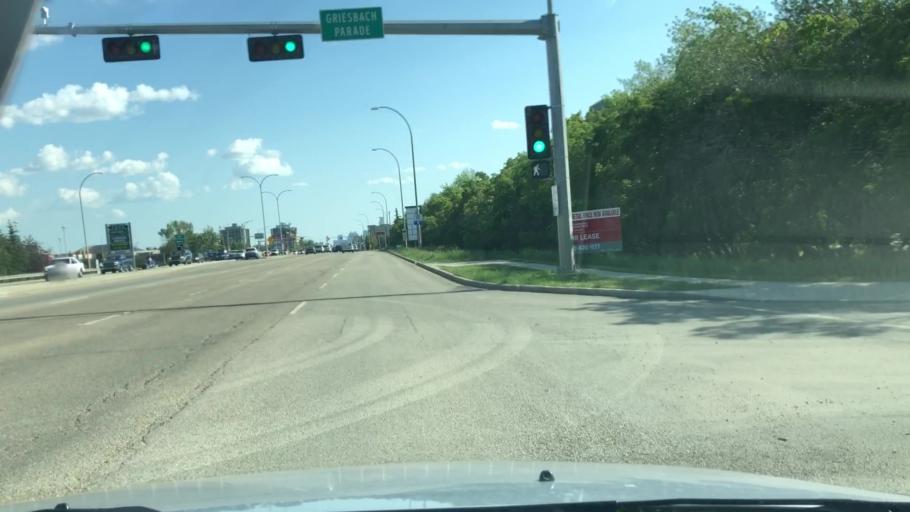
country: CA
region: Alberta
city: Edmonton
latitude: 53.6025
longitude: -113.4922
